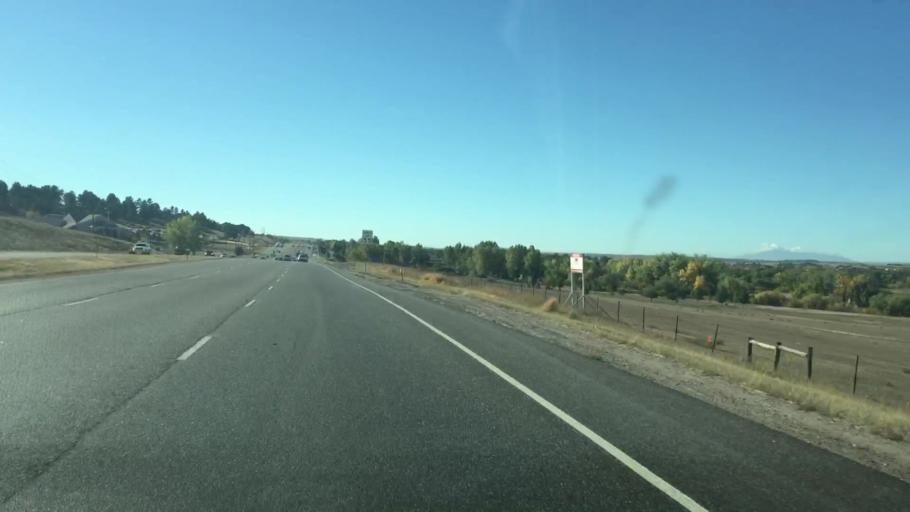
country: US
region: Colorado
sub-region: Douglas County
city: Parker
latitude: 39.5064
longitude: -104.7633
